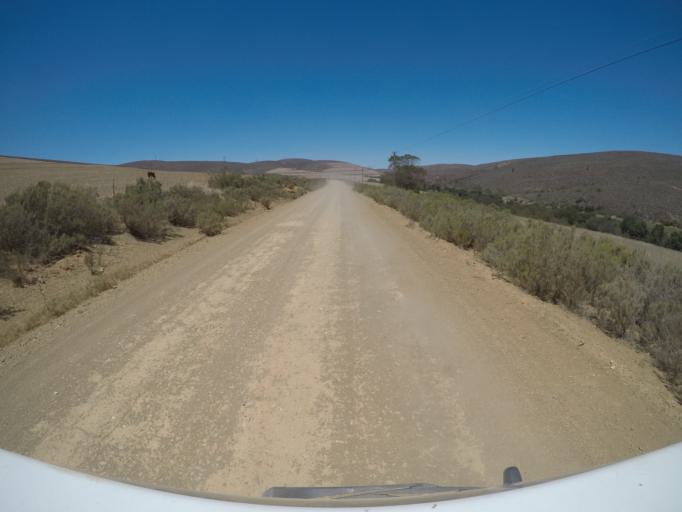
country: ZA
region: Western Cape
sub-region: Overberg District Municipality
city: Caledon
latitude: -34.1332
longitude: 19.2426
